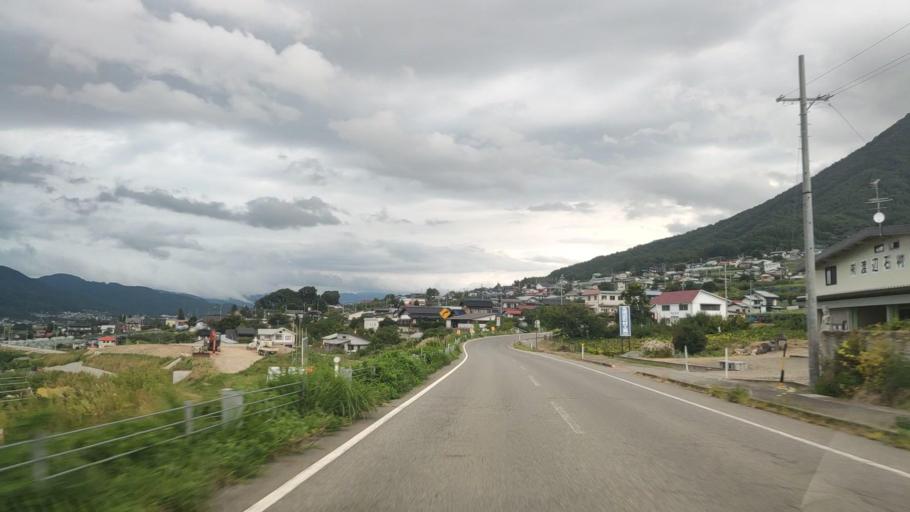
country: JP
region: Nagano
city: Nakano
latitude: 36.7951
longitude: 138.3610
